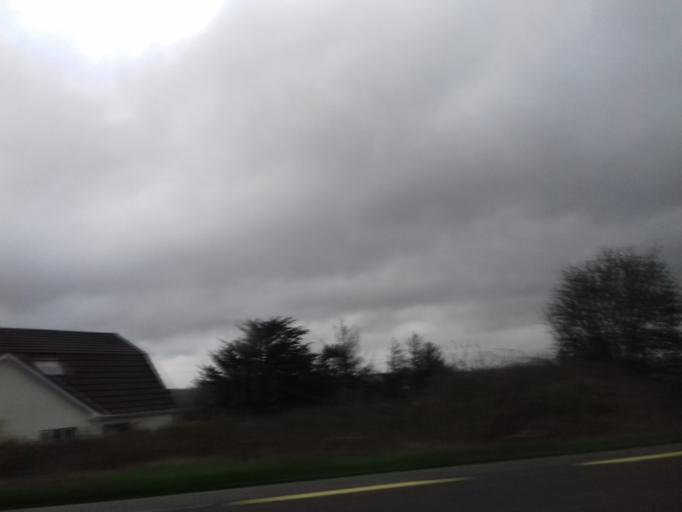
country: IE
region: Munster
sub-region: County Limerick
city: Abbeyfeale
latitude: 52.3648
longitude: -9.3240
